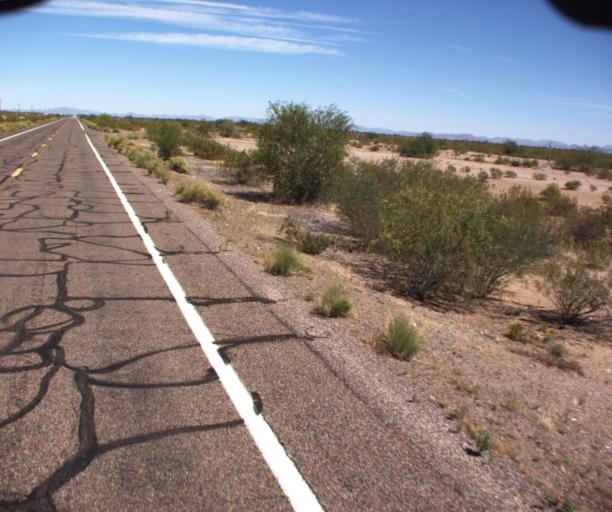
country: US
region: Arizona
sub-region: Maricopa County
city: Gila Bend
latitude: 32.8109
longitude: -112.7935
